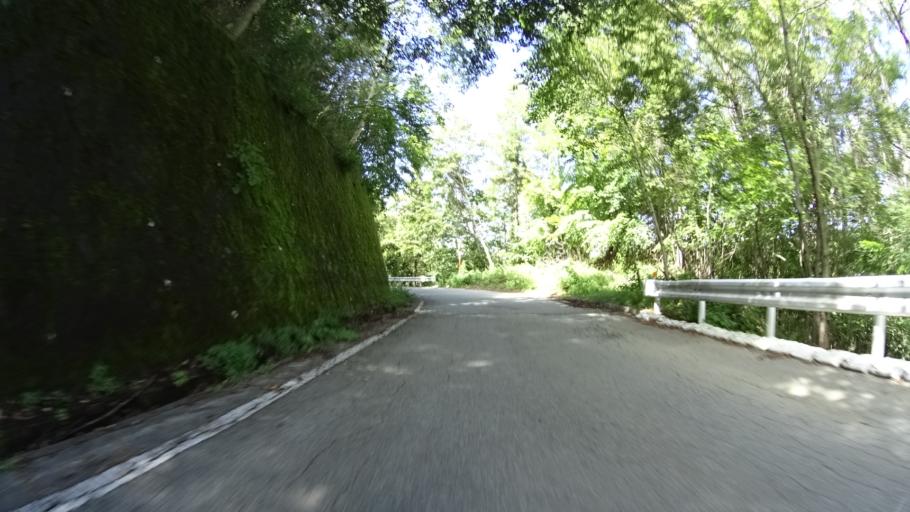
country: JP
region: Yamanashi
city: Enzan
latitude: 35.7178
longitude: 138.8391
